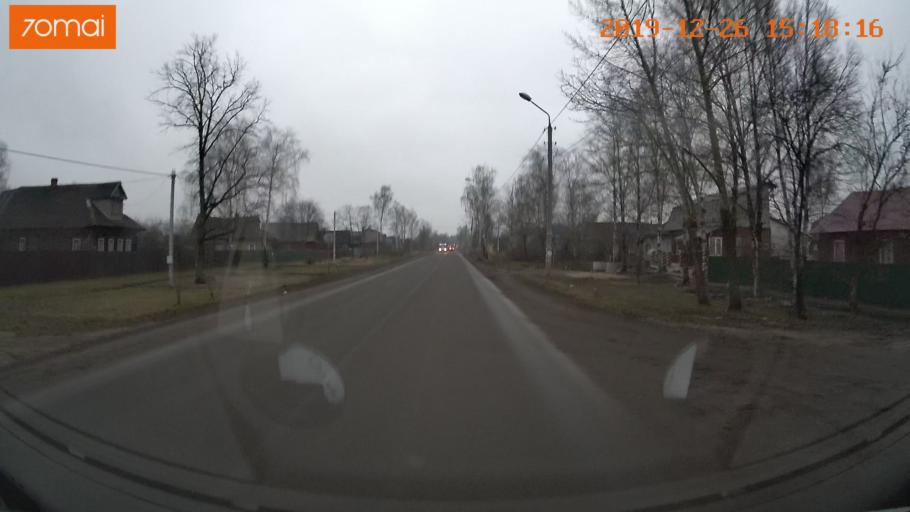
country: RU
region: Jaroslavl
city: Rybinsk
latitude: 58.0708
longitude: 38.8437
